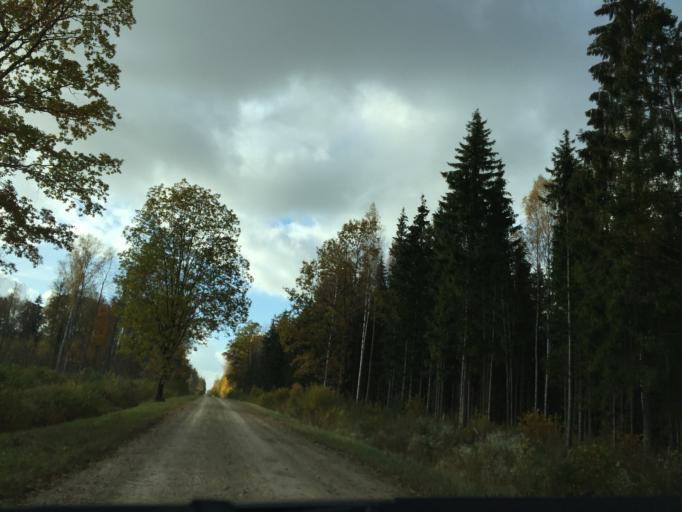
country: LV
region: Ogre
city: Jumprava
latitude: 56.7394
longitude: 24.9228
